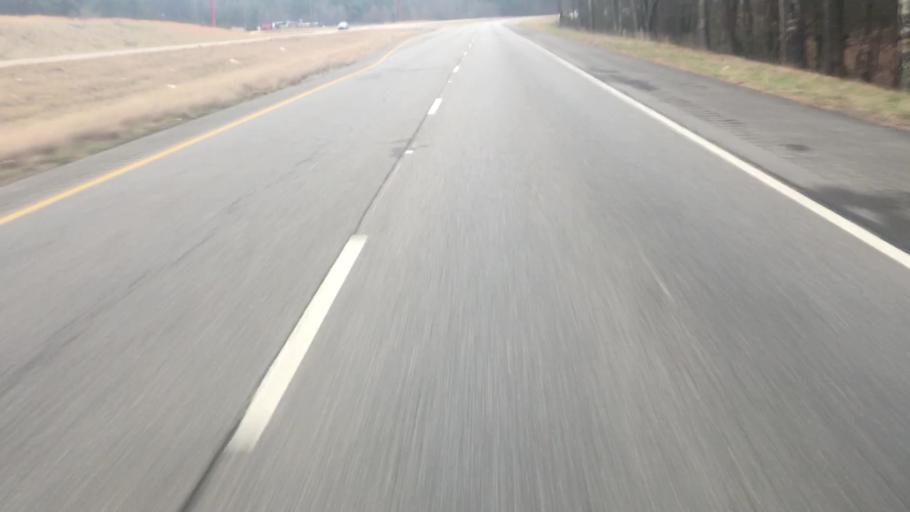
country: US
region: Alabama
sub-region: Walker County
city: Sumiton
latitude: 33.7752
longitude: -87.0771
